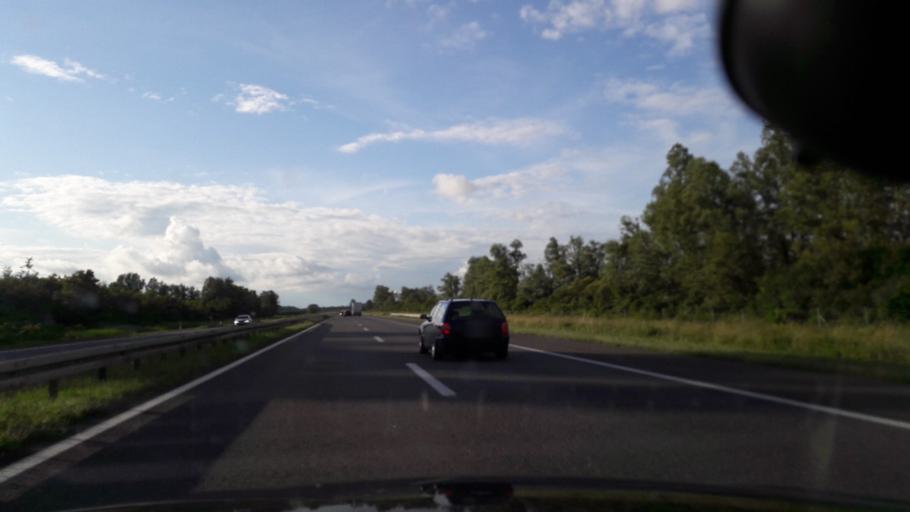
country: HR
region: Zagrebacka
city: Novoselec
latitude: 45.5895
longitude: 16.5577
